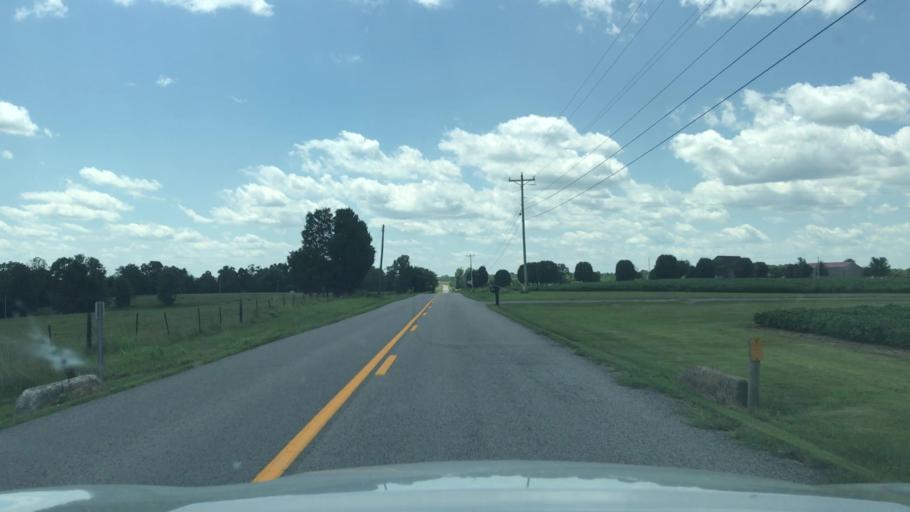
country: US
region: Kentucky
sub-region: Christian County
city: Hopkinsville
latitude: 36.9682
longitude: -87.3807
